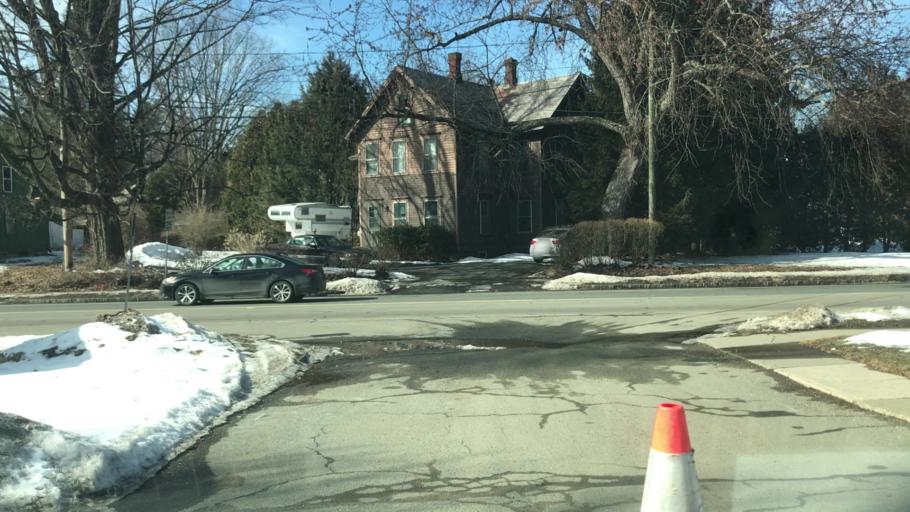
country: US
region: Massachusetts
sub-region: Franklin County
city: Greenfield
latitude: 42.5843
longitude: -72.6039
